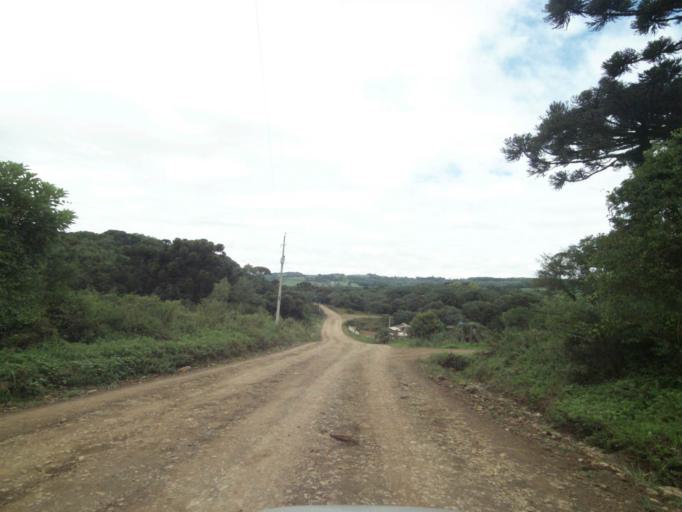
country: BR
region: Rio Grande do Sul
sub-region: Lagoa Vermelha
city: Lagoa Vermelha
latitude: -28.2257
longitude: -51.5381
